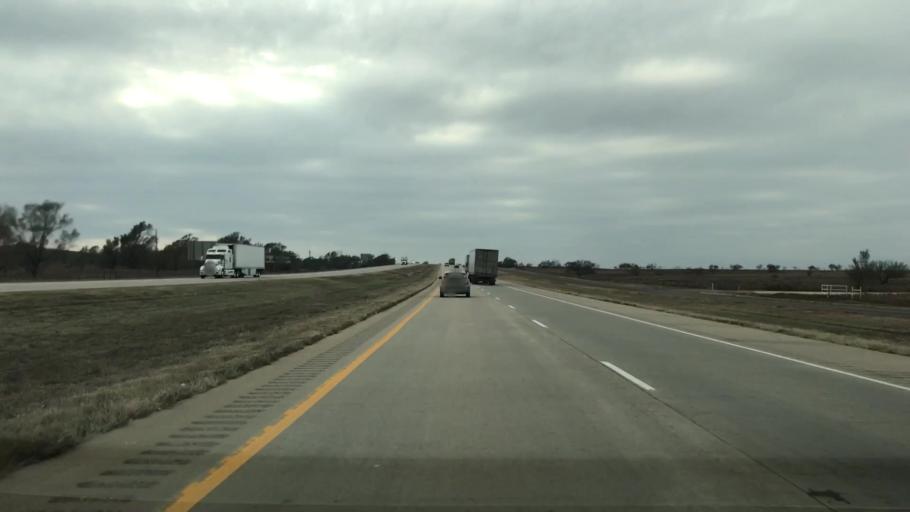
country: US
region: Texas
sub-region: Wheeler County
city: Shamrock
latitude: 35.2293
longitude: -100.2625
